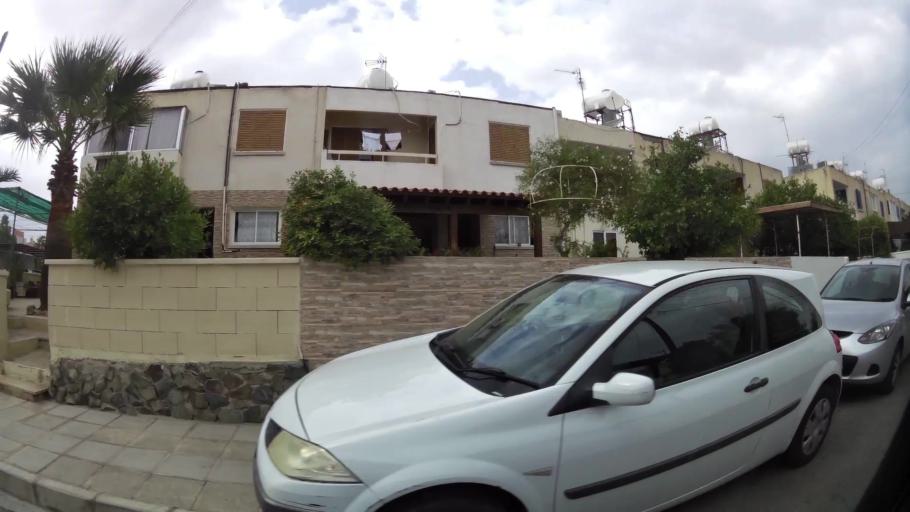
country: CY
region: Lefkosia
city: Geri
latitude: 35.1162
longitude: 33.3847
